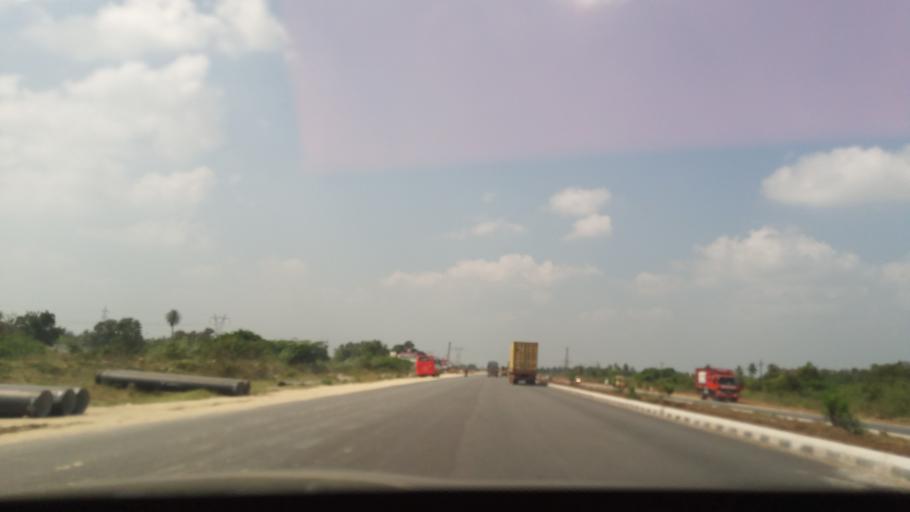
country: IN
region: Tamil Nadu
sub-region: Vellore
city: Walajapet
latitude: 12.8977
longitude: 79.5233
